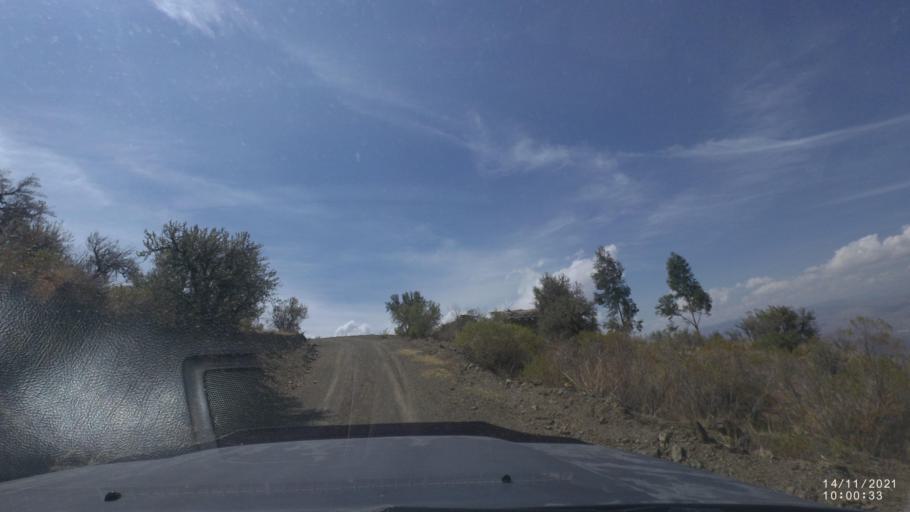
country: BO
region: Cochabamba
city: Cochabamba
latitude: -17.3530
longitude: -66.0899
